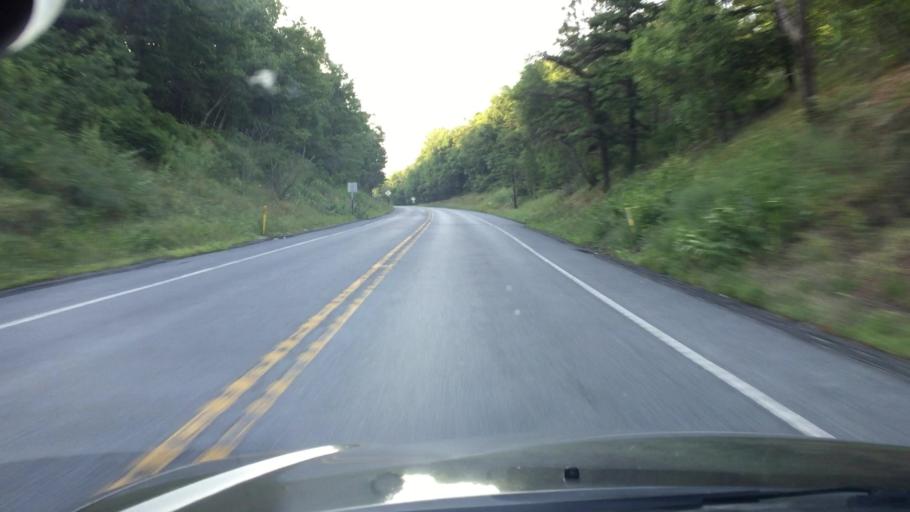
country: US
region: Pennsylvania
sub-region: Carbon County
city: Nesquehoning
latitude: 40.8849
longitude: -75.8010
